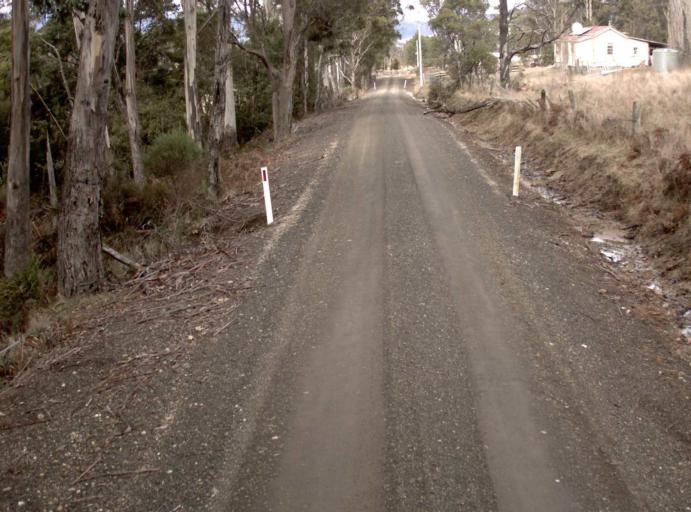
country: AU
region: Tasmania
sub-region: Northern Midlands
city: Evandale
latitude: -41.4563
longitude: 147.4452
